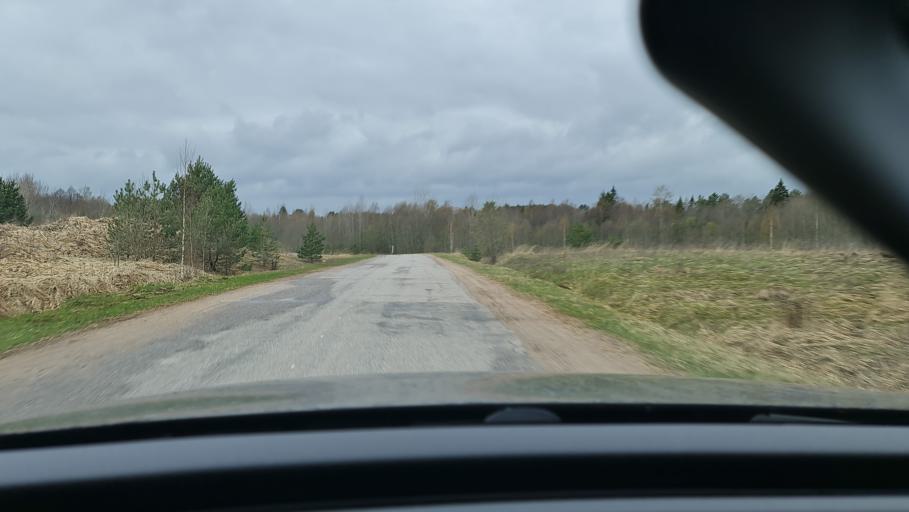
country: RU
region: Novgorod
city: Marevo
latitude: 57.1084
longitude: 31.7769
